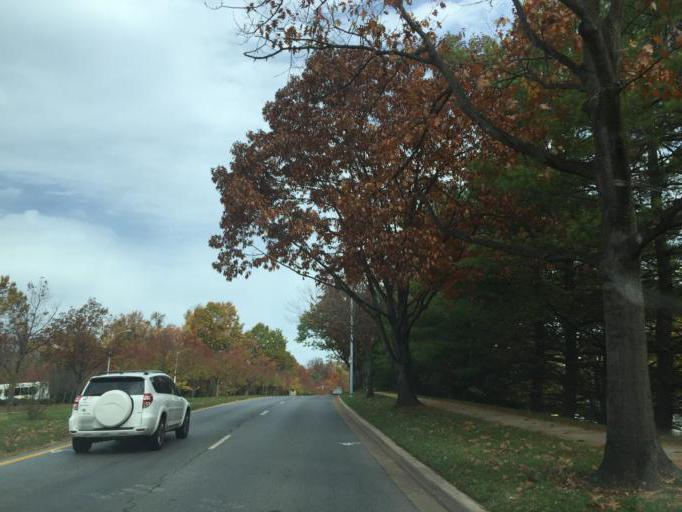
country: US
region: Maryland
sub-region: Montgomery County
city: Germantown
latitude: 39.1898
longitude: -77.2731
